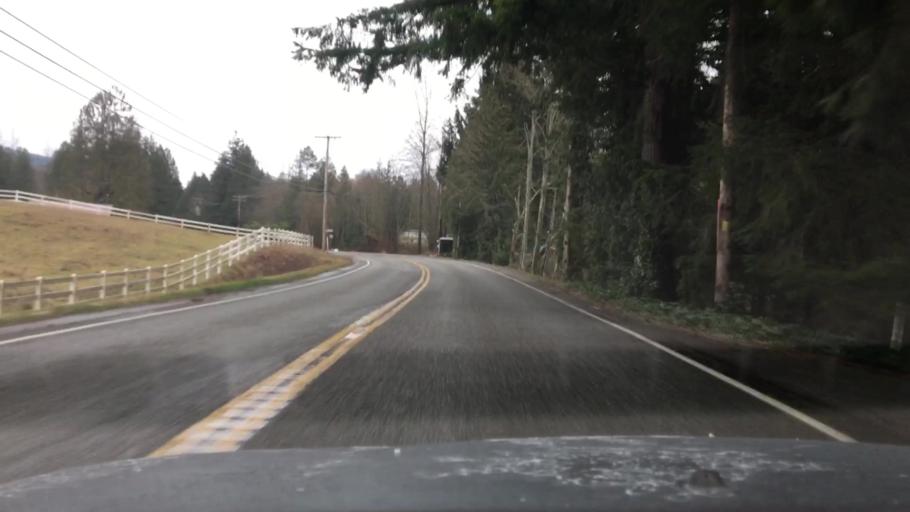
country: US
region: Washington
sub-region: Whatcom County
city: Sudden Valley
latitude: 48.6474
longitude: -122.3242
